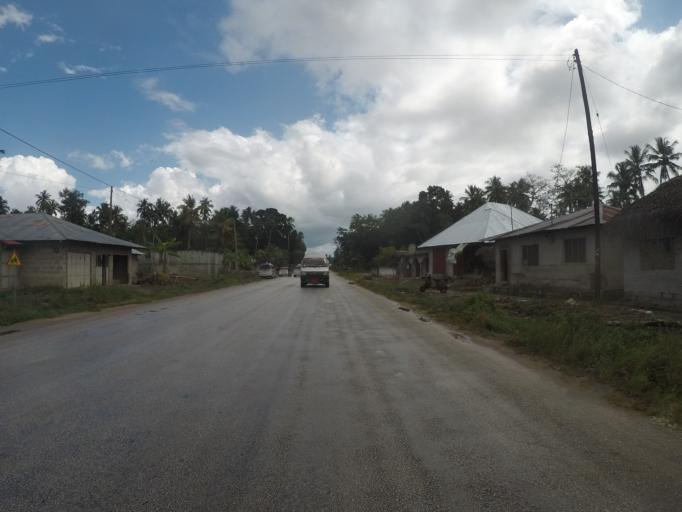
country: TZ
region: Zanzibar Central/South
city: Koani
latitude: -6.0213
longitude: 39.2417
